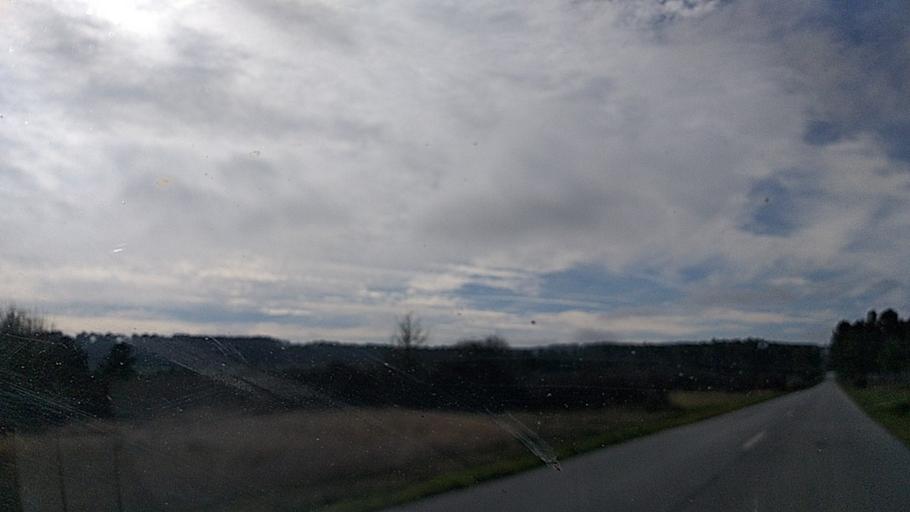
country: PT
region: Guarda
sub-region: Fornos de Algodres
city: Fornos de Algodres
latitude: 40.6702
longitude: -7.5291
